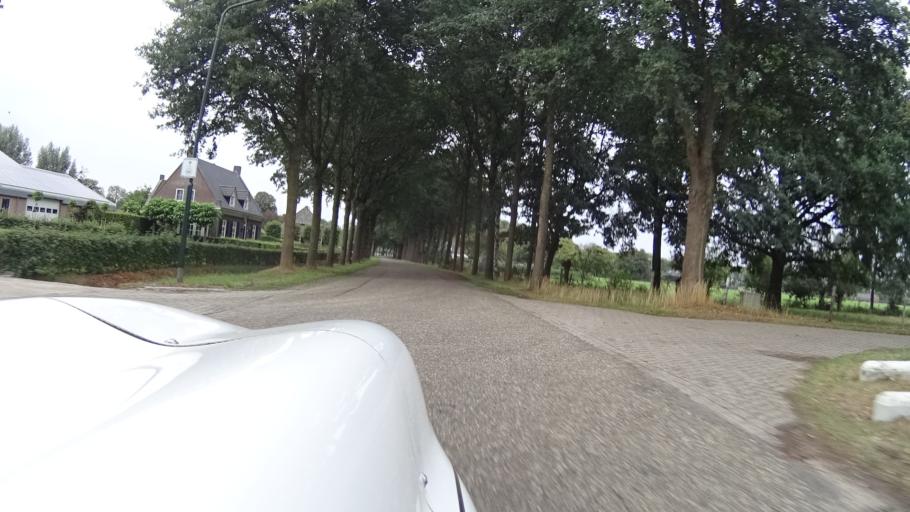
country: NL
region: North Brabant
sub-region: Gemeente Veghel
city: Erp
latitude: 51.6059
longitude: 5.6175
